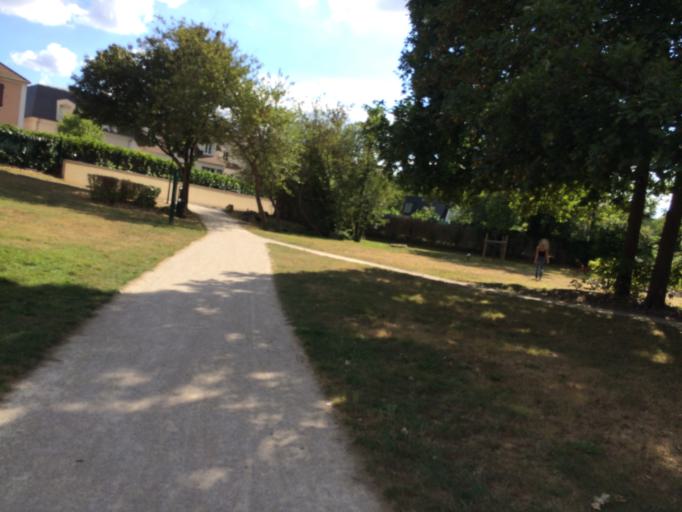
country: FR
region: Ile-de-France
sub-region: Departement de l'Essonne
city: Villebon-sur-Yvette
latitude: 48.7017
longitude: 2.2398
